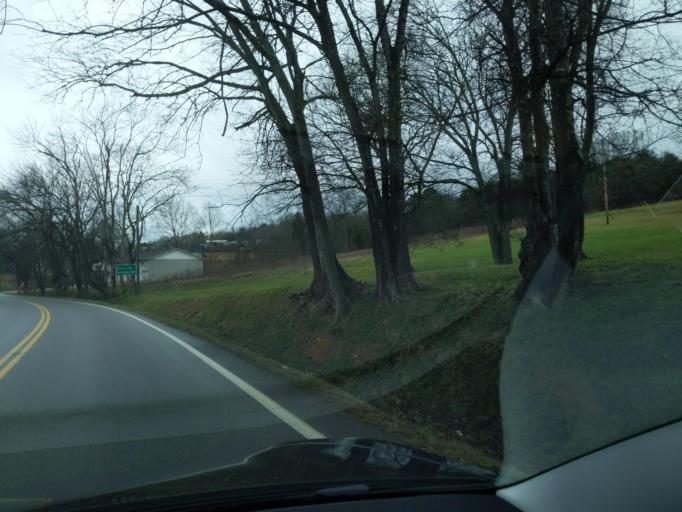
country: US
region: Tennessee
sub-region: Sevier County
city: Sevierville
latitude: 35.9732
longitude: -83.5406
